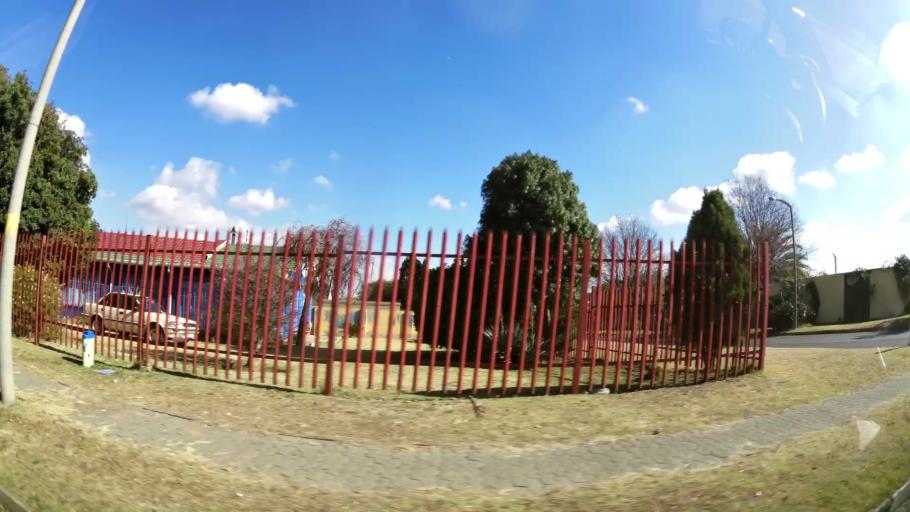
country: ZA
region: Gauteng
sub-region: City of Johannesburg Metropolitan Municipality
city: Roodepoort
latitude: -26.1404
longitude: 27.8276
